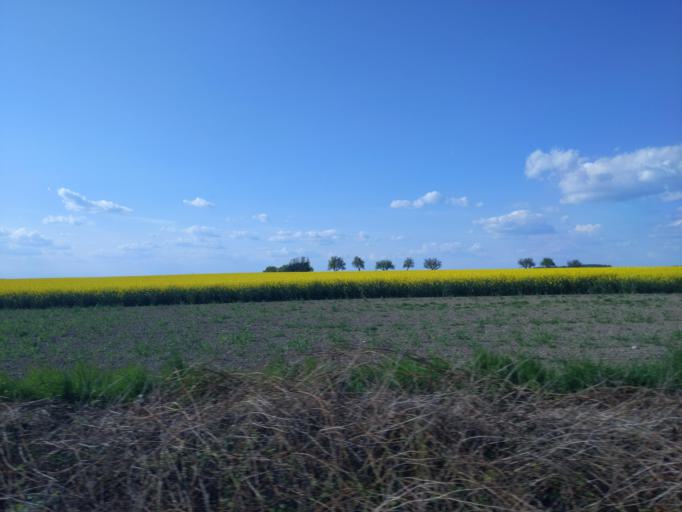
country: DE
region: Saxony
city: Goda
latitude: 51.1593
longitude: 14.3419
